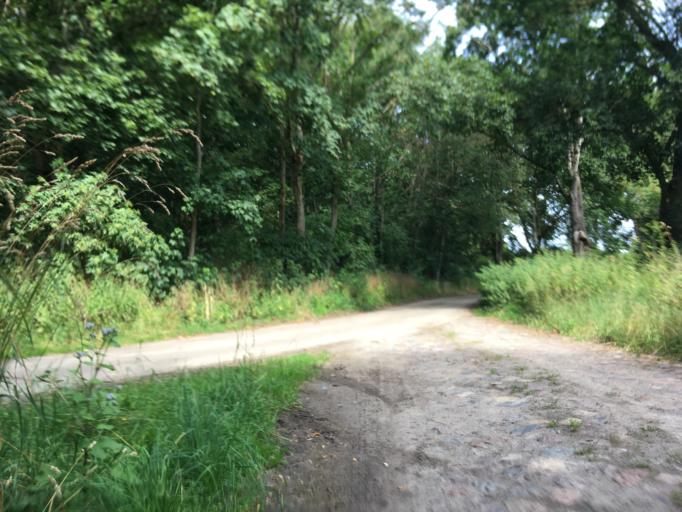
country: DE
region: Brandenburg
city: Zichow
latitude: 53.1897
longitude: 14.0750
